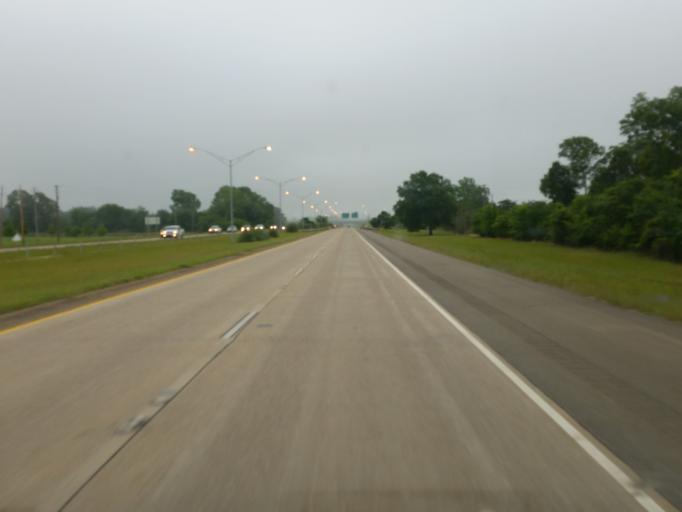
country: US
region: Louisiana
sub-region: Bossier Parish
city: Red Chute
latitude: 32.5363
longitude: -93.6430
